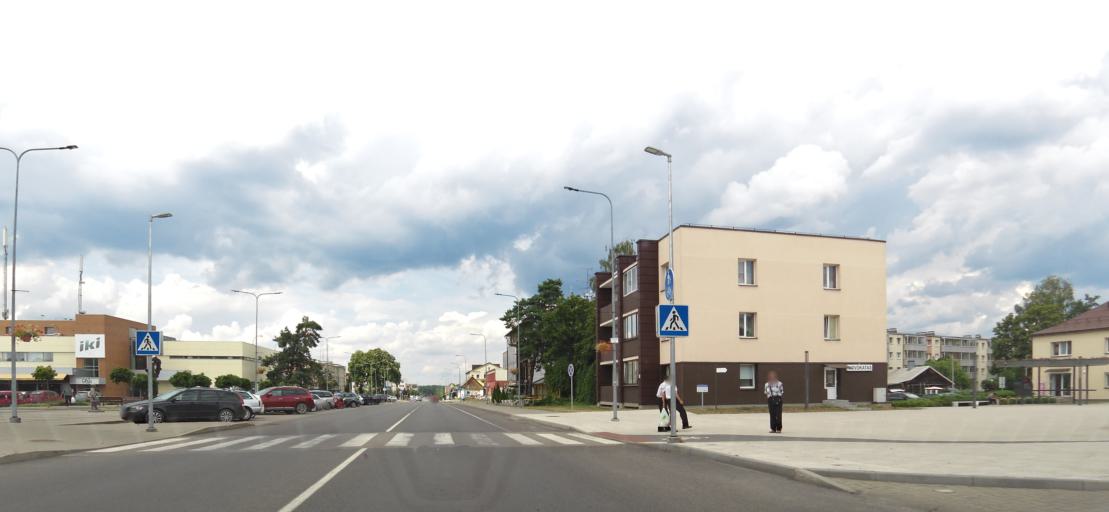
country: LT
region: Alytaus apskritis
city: Varena
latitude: 54.2109
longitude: 24.5711
